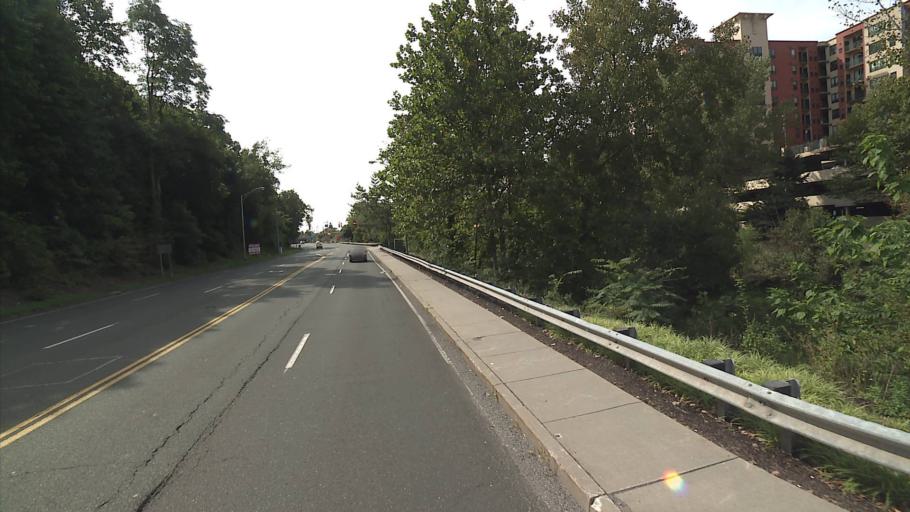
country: US
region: Connecticut
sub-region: Fairfield County
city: Norwalk
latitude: 41.1460
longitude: -73.4265
